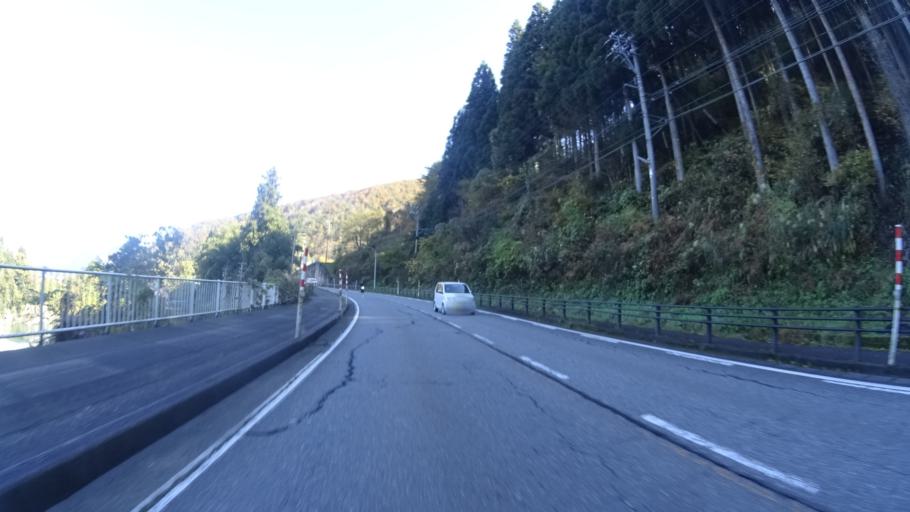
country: JP
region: Ishikawa
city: Tsurugi-asahimachi
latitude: 36.4014
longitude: 136.6291
